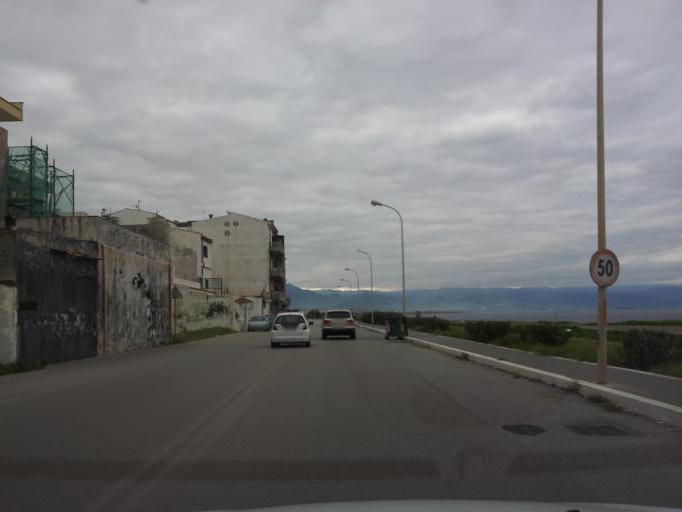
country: IT
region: Sicily
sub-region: Messina
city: Milazzo
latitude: 38.2094
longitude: 15.2289
